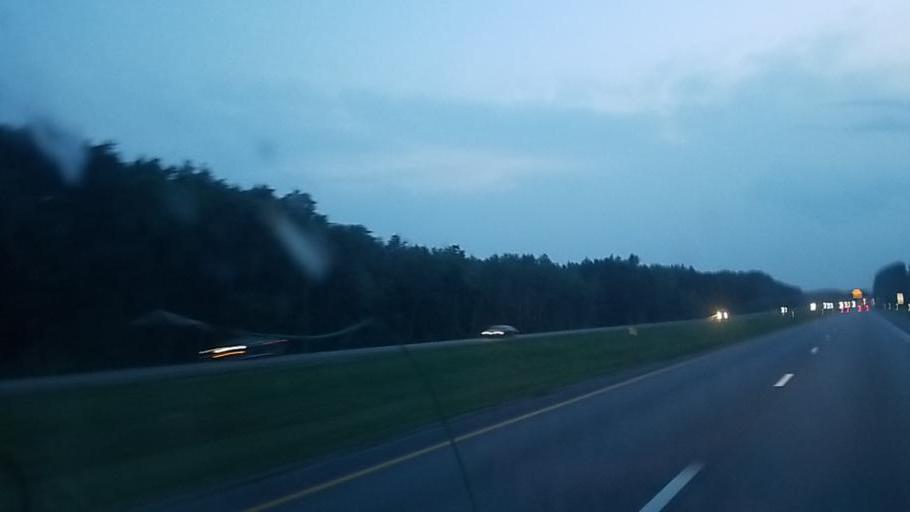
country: US
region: New York
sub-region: Onondaga County
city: Minoa
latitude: 43.0921
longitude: -75.9466
